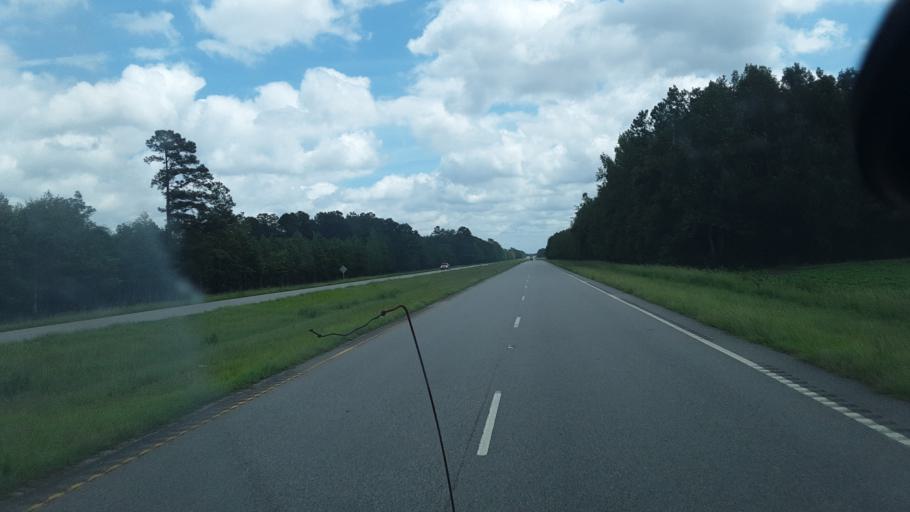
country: US
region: South Carolina
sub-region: Horry County
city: Loris
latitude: 34.0927
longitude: -78.9059
